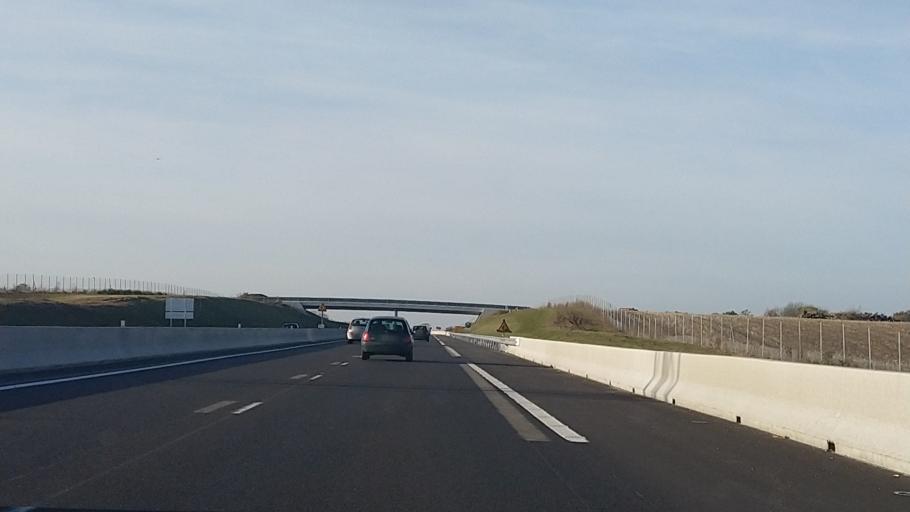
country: FR
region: Ile-de-France
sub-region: Departement du Val-d'Oise
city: Montsoult
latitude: 49.0841
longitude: 2.3221
